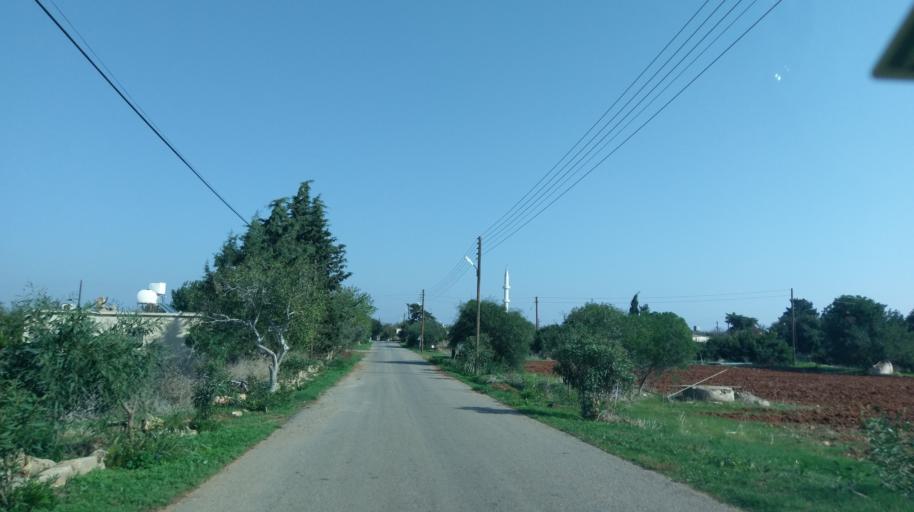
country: CY
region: Ammochostos
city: Leonarisso
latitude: 35.4693
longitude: 34.2113
